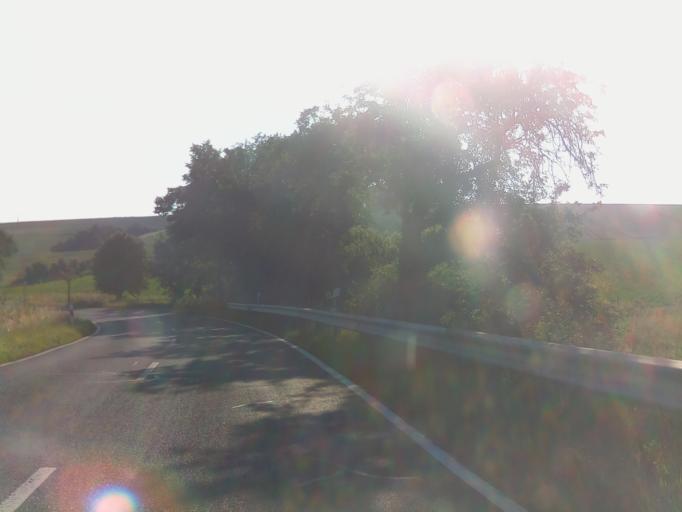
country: DE
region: Lower Saxony
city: Baddeckenstedt
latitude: 52.0859
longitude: 10.2065
